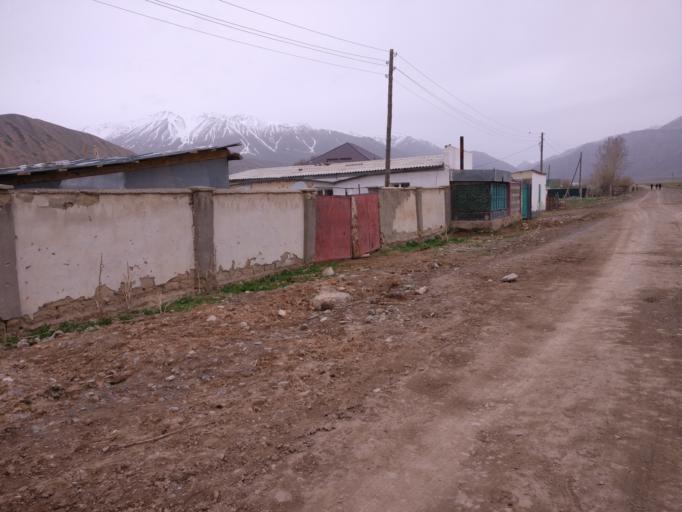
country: KG
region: Naryn
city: Naryn
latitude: 41.5161
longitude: 76.4403
